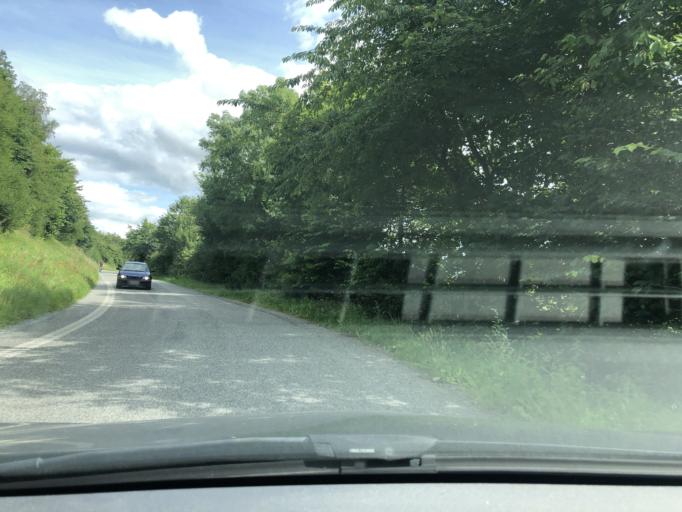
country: DK
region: South Denmark
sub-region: Vejle Kommune
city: Jelling
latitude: 55.6974
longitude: 9.4470
